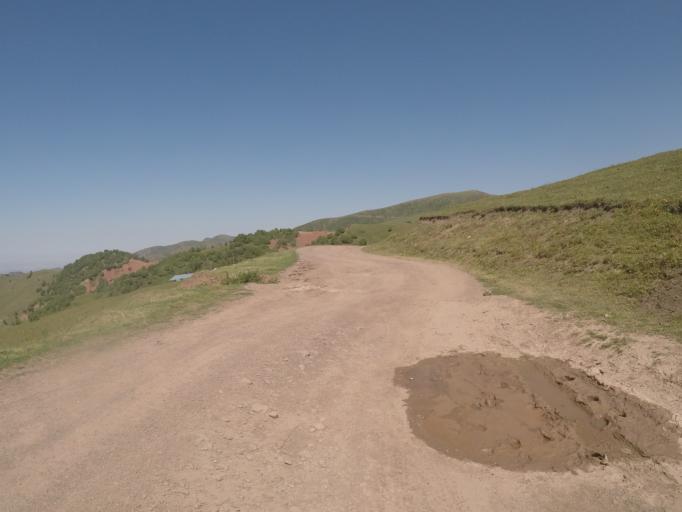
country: KG
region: Chuy
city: Bishkek
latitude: 42.6470
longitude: 74.5641
